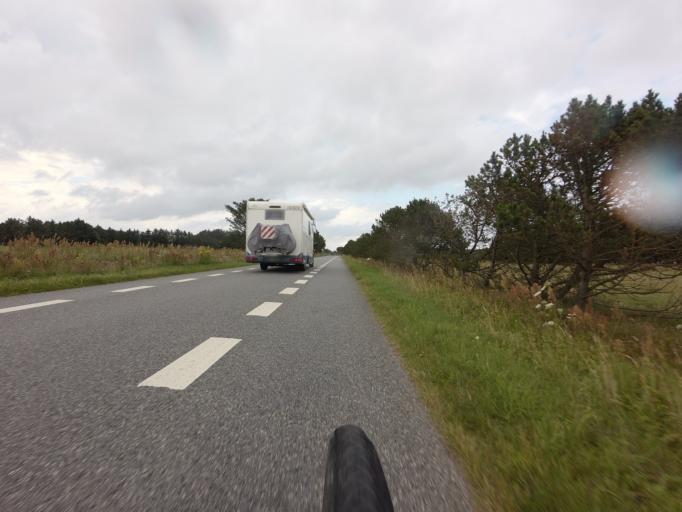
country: DK
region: North Denmark
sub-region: Hjorring Kommune
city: Hjorring
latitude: 57.4601
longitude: 9.7971
